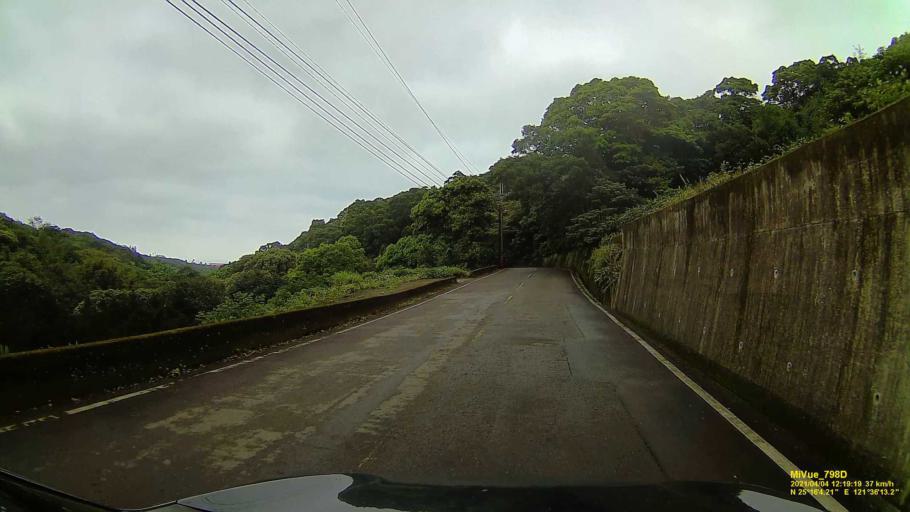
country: TW
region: Taiwan
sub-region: Keelung
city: Keelung
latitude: 25.2681
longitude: 121.6038
